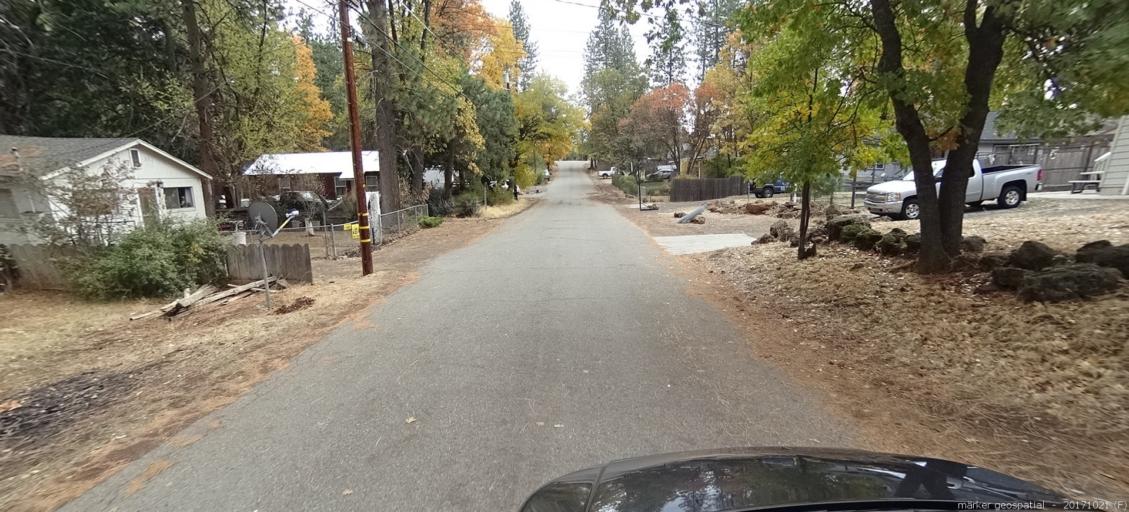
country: US
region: California
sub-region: Shasta County
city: Burney
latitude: 40.9181
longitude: -121.6293
